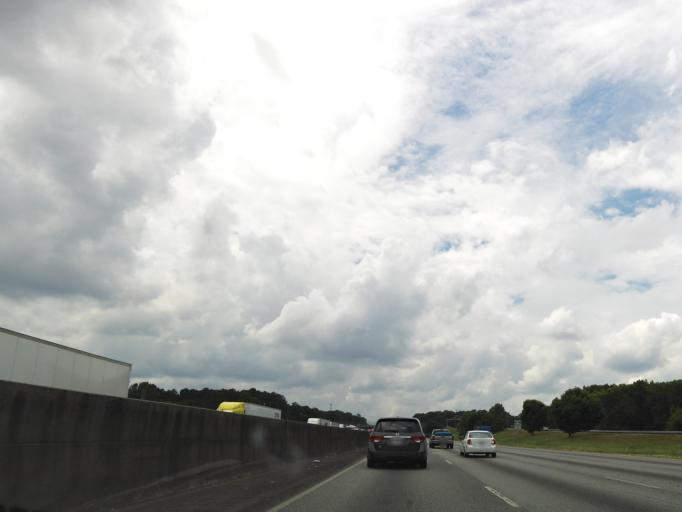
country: US
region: Georgia
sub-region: Cobb County
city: Mableton
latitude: 33.7735
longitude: -84.5561
